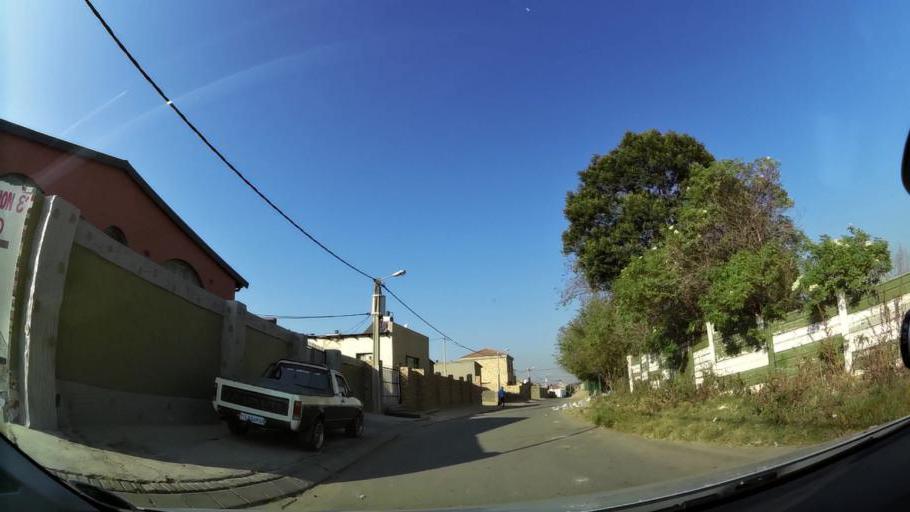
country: ZA
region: Gauteng
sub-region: City of Johannesburg Metropolitan Municipality
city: Modderfontein
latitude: -26.0913
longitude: 28.1108
